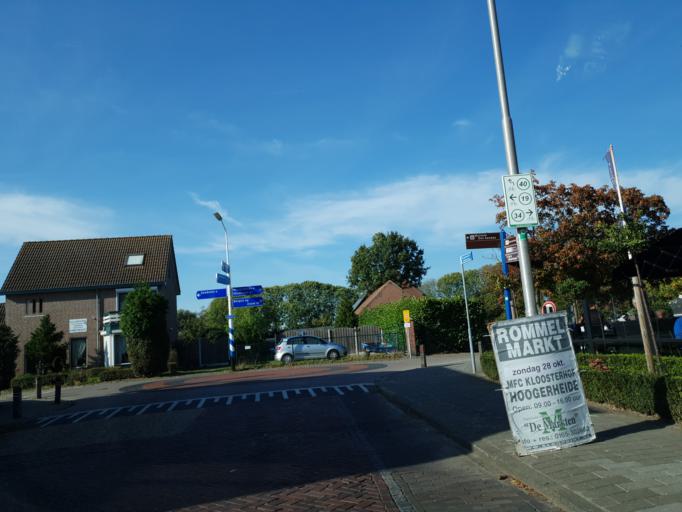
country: NL
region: North Brabant
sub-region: Gemeente Woensdrecht
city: Woensdrecht
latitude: 51.3936
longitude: 4.3151
